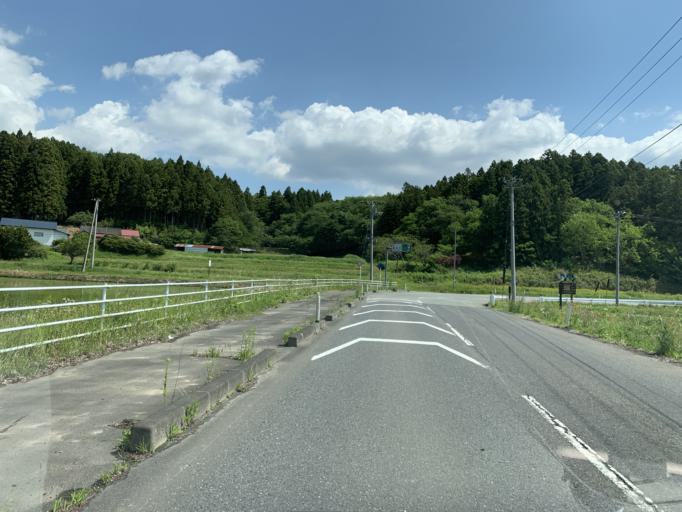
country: JP
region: Miyagi
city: Furukawa
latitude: 38.6866
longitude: 140.9688
